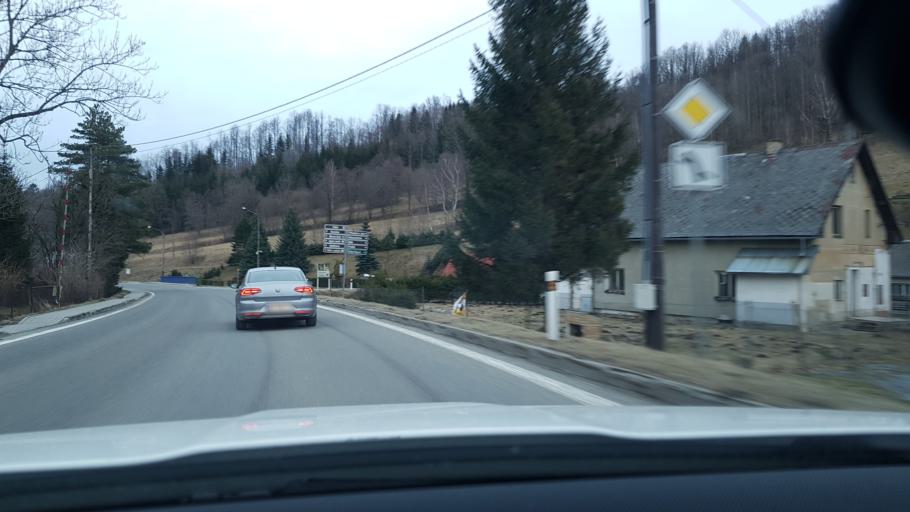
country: CZ
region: Olomoucky
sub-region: Okres Jesenik
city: Jesenik
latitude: 50.1623
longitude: 17.1961
